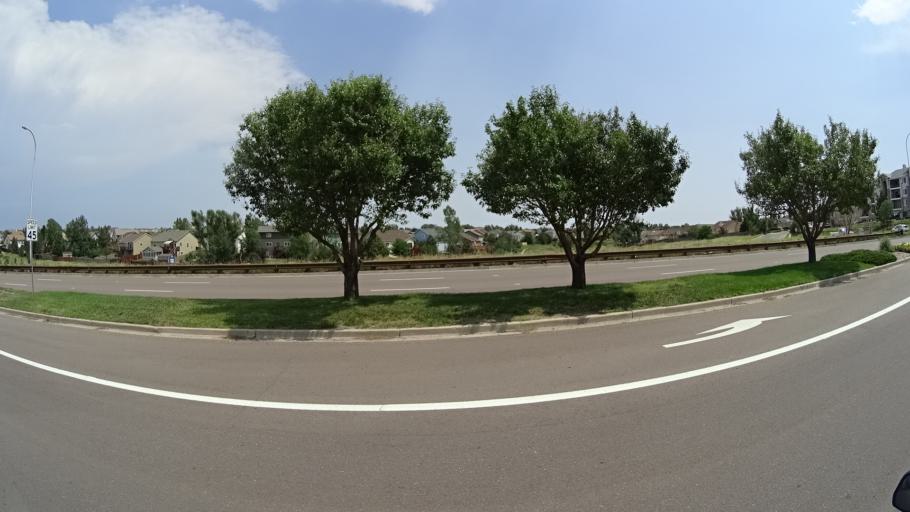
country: US
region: Colorado
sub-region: El Paso County
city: Cimarron Hills
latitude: 38.9256
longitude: -104.7389
